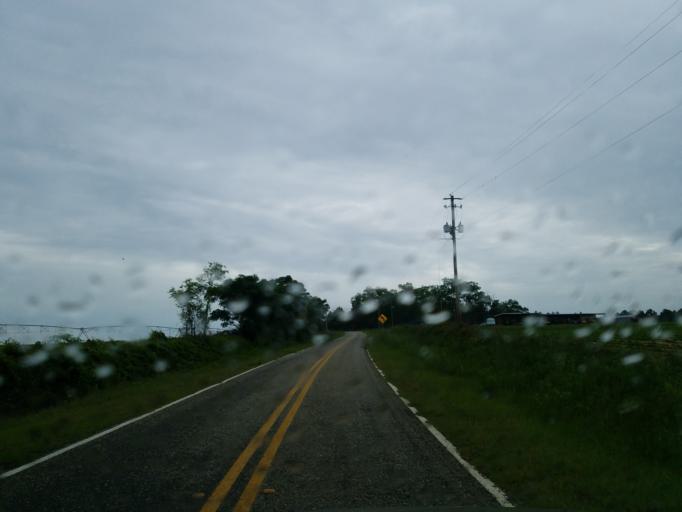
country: US
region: Georgia
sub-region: Crisp County
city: Cordele
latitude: 31.9393
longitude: -83.7004
